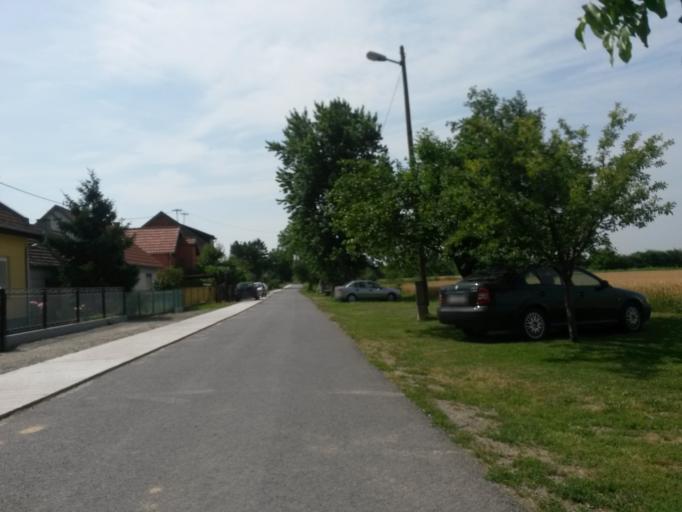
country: HR
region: Osjecko-Baranjska
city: Brijest
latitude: 45.5408
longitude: 18.6630
